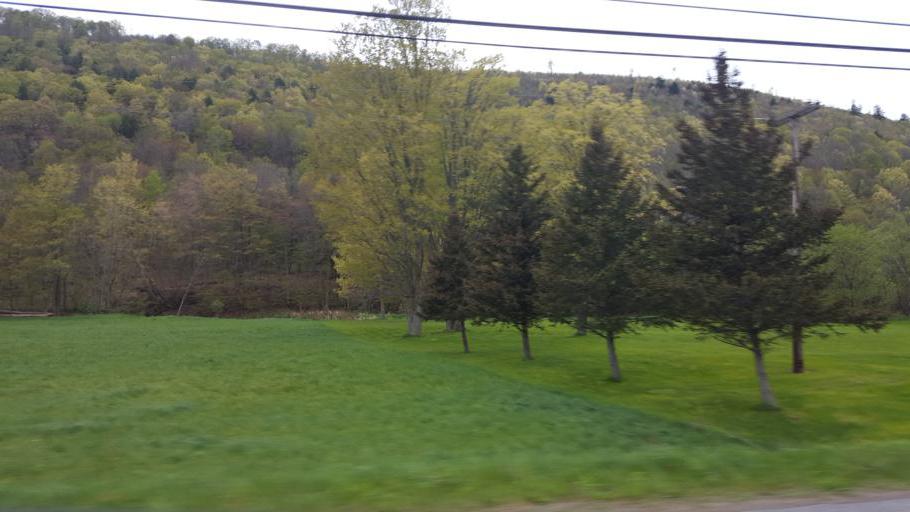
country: US
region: Pennsylvania
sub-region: Tioga County
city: Westfield
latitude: 41.9367
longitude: -77.6421
